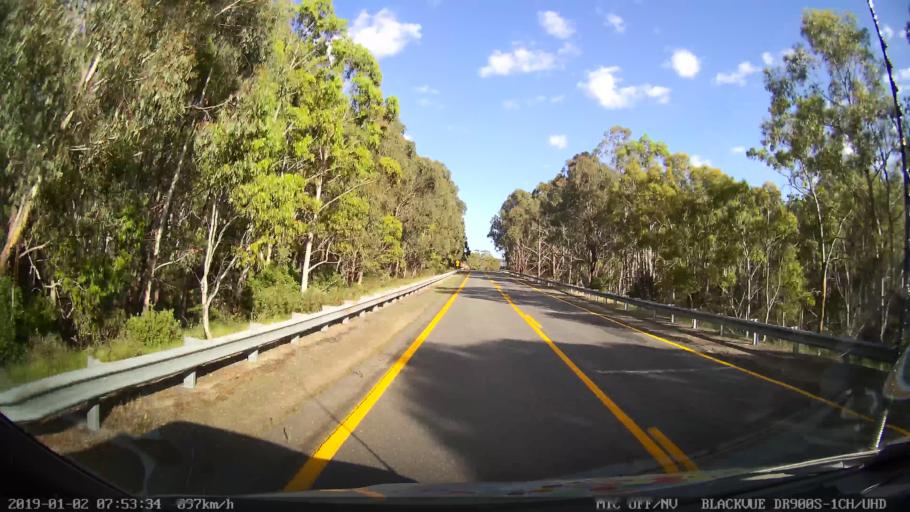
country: AU
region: New South Wales
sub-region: Tumut Shire
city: Tumut
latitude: -35.7038
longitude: 148.5047
